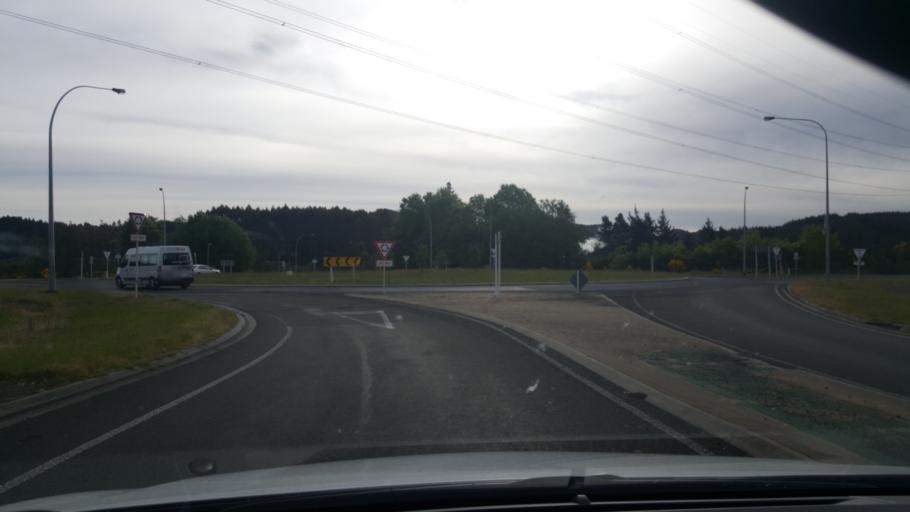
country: NZ
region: Waikato
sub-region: Taupo District
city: Taupo
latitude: -38.6234
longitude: 176.1007
